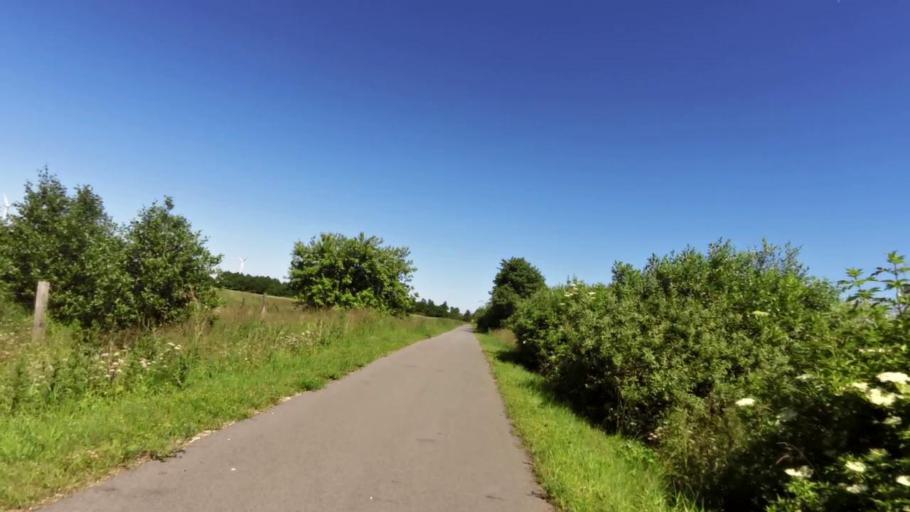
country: PL
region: West Pomeranian Voivodeship
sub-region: Powiat kolobrzeski
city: Dygowo
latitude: 54.0461
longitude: 15.7400
